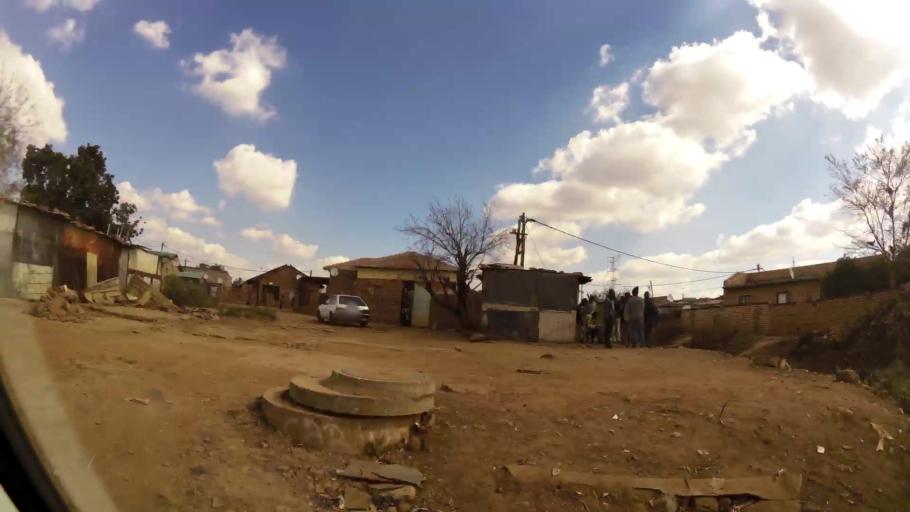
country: ZA
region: Gauteng
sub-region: City of Tshwane Metropolitan Municipality
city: Cullinan
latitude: -25.7076
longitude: 28.3978
